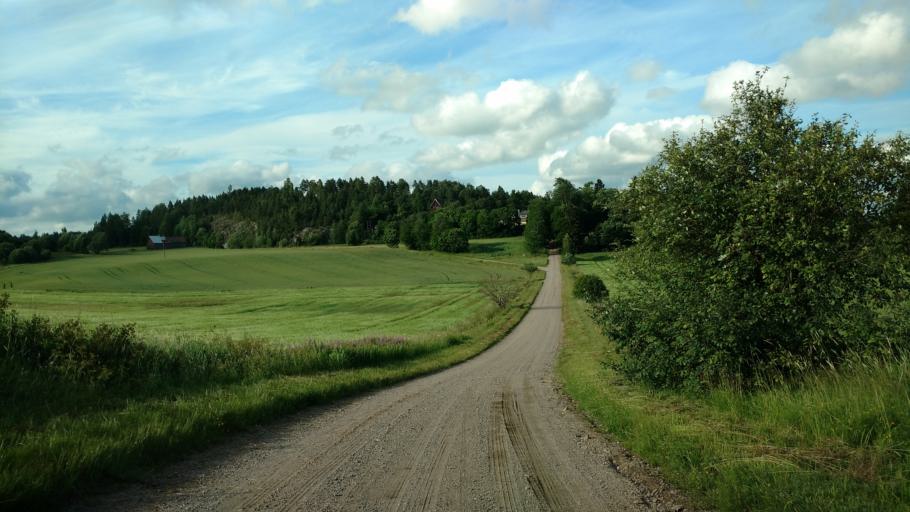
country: FI
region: Varsinais-Suomi
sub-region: Salo
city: Salo
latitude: 60.4221
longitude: 23.1748
